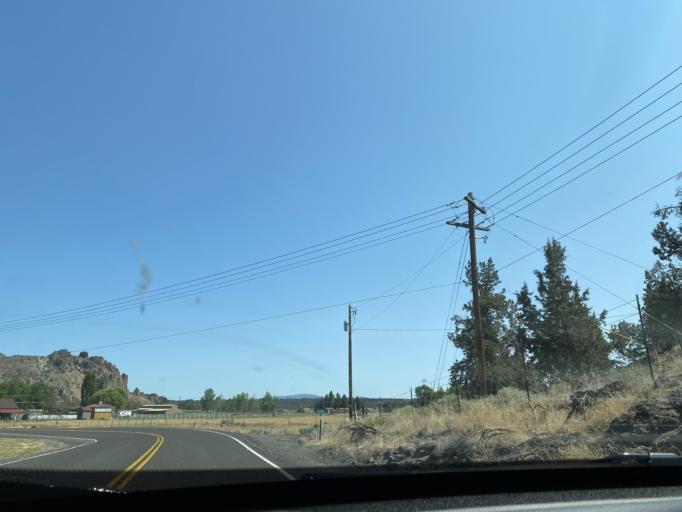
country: US
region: Oregon
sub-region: Deschutes County
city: Terrebonne
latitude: 44.3672
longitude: -121.1629
